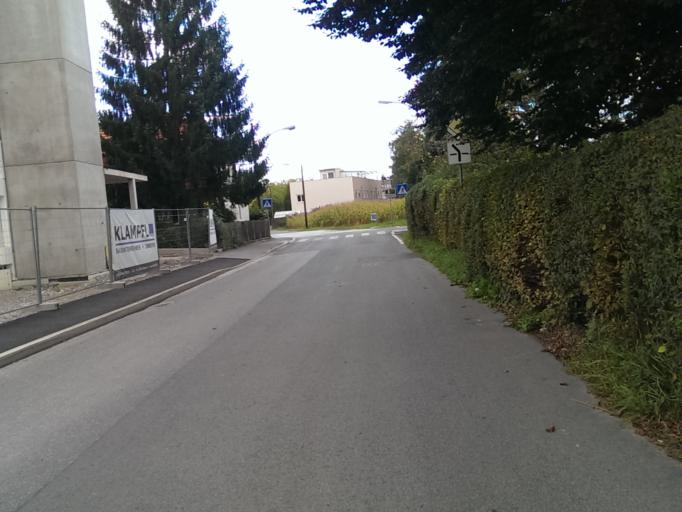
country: AT
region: Styria
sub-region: Graz Stadt
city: Graz
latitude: 47.0539
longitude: 15.4689
